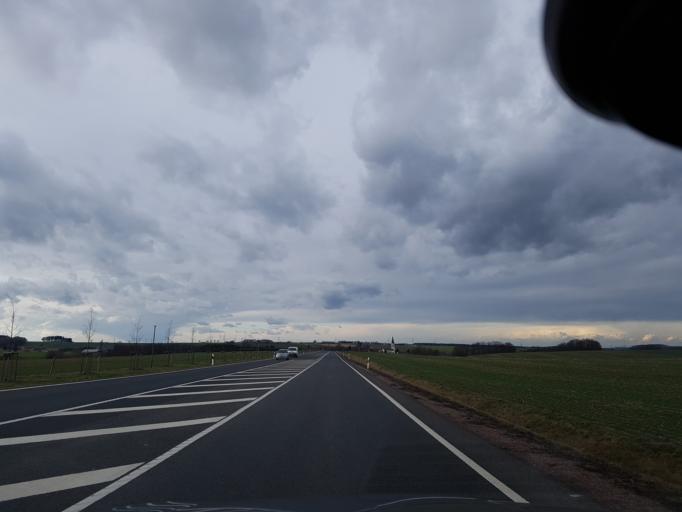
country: DE
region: Saxony
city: Hainichen
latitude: 51.0169
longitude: 13.1249
